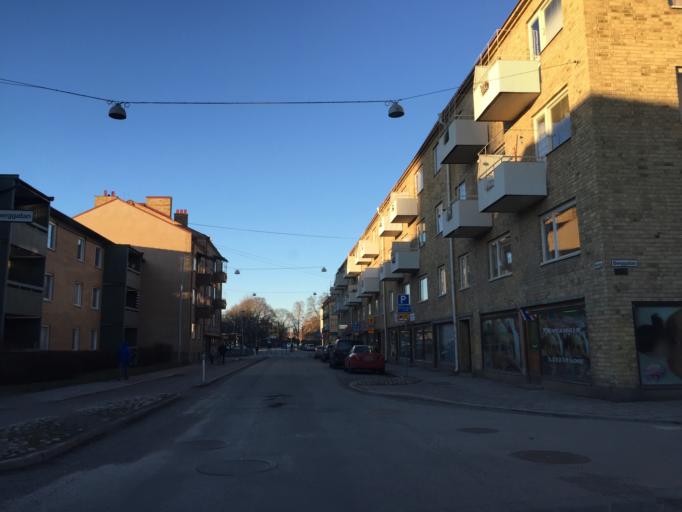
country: SE
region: OErebro
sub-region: Orebro Kommun
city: Orebro
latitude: 59.2804
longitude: 15.2234
